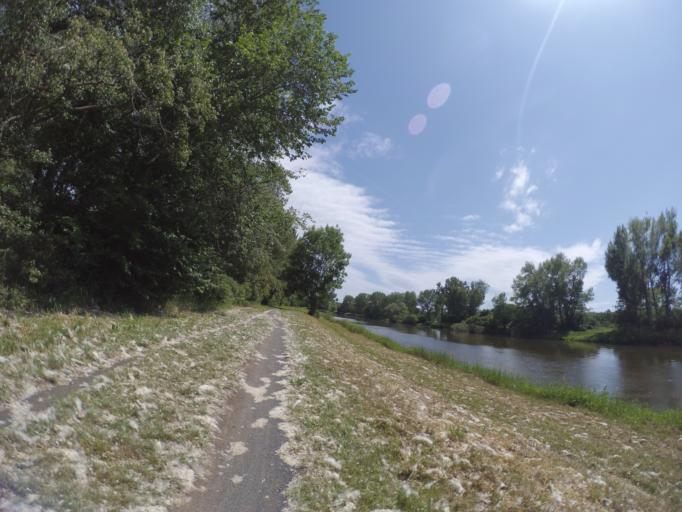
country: CZ
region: Central Bohemia
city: Milovice
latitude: 50.1695
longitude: 14.9059
